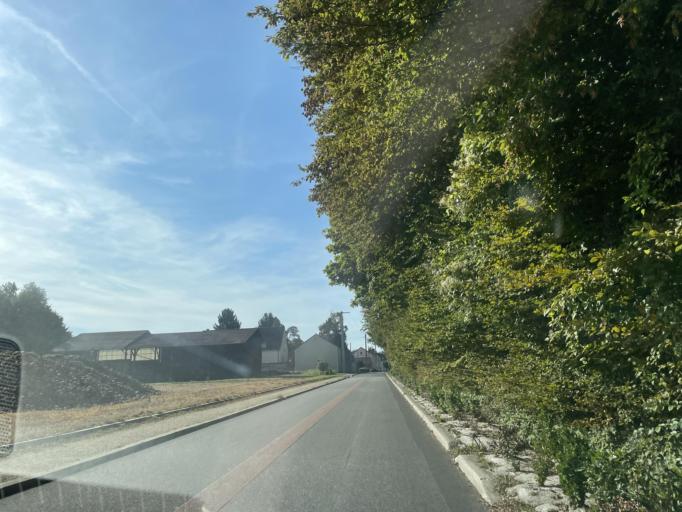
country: FR
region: Ile-de-France
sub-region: Departement de Seine-et-Marne
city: Saint-Jean-les-Deux-Jumeaux
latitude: 48.9448
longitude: 2.9894
